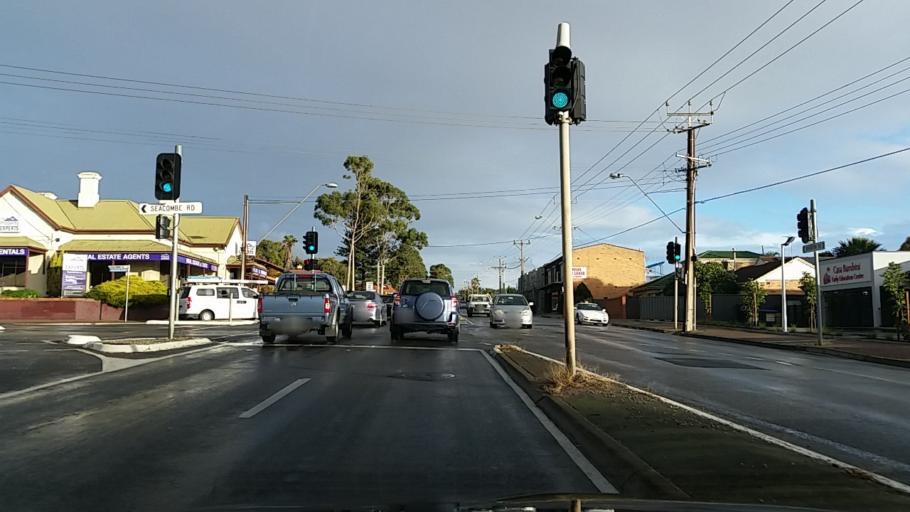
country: AU
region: South Australia
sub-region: Adelaide Hills
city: Seacliff
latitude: -35.0300
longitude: 138.5239
